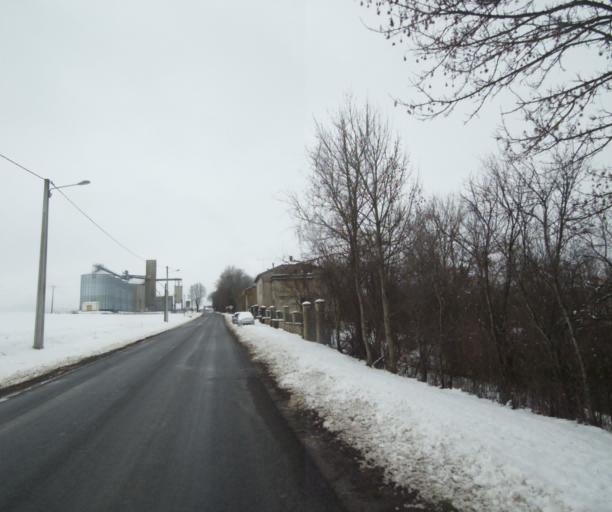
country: FR
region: Champagne-Ardenne
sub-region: Departement de la Haute-Marne
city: Wassy
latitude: 48.4360
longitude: 4.9608
